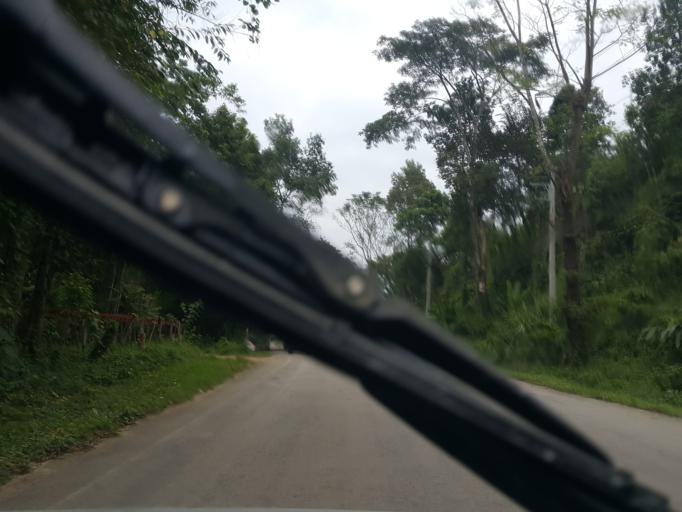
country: TH
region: Chiang Mai
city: Mae Taeng
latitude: 19.1208
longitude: 98.7375
